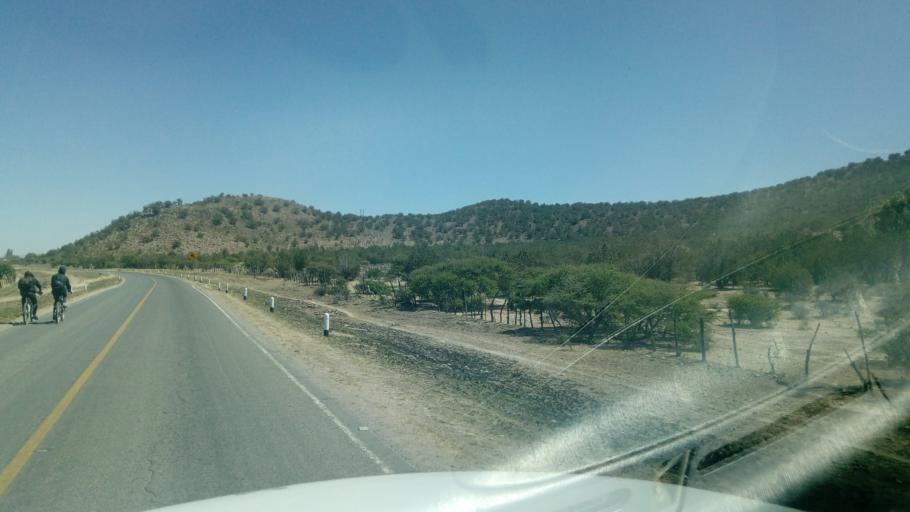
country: MX
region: Durango
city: Victoria de Durango
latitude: 24.1597
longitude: -104.7042
